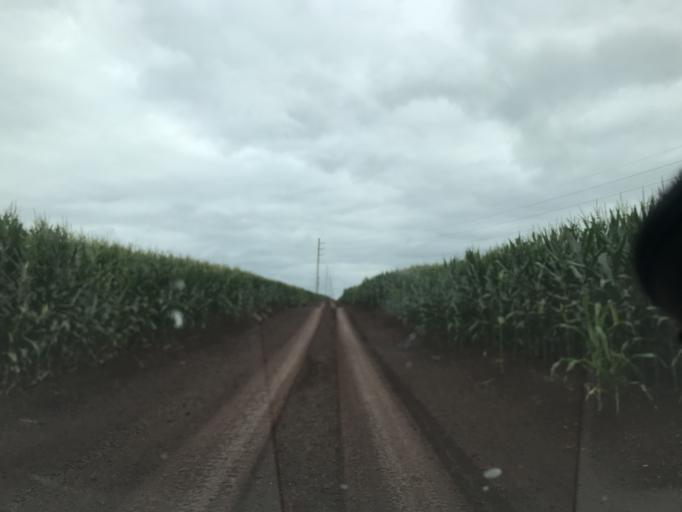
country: BR
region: Parana
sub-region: Palotina
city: Palotina
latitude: -24.2983
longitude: -53.8166
